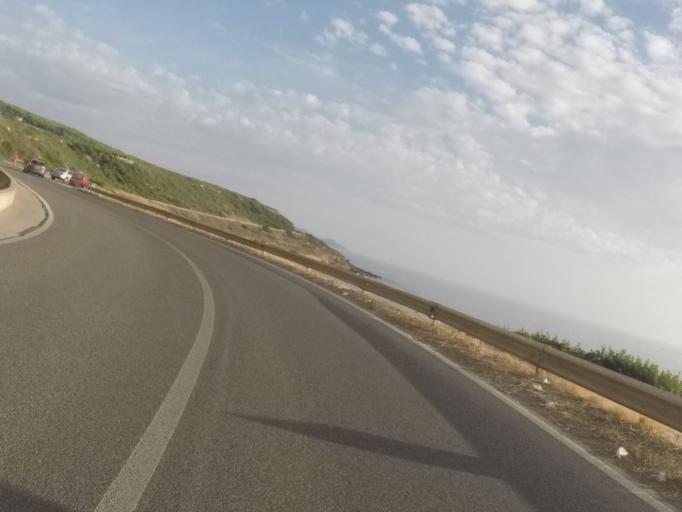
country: IT
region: Sardinia
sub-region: Provincia di Sassari
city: Alghero
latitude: 40.5418
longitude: 8.3219
